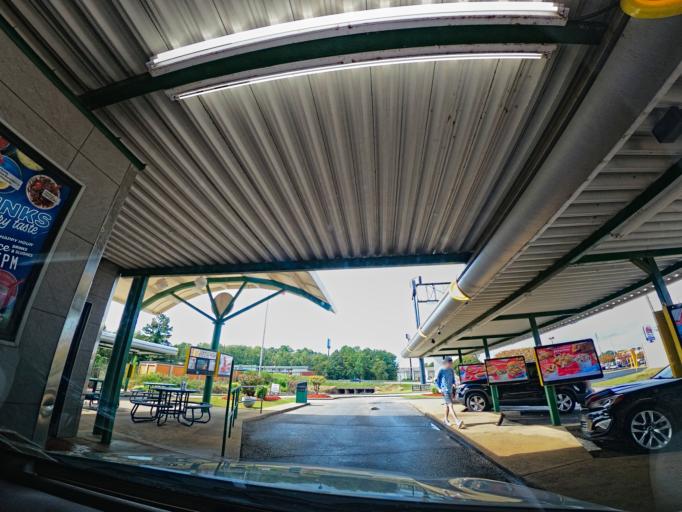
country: US
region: Alabama
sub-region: Tuscaloosa County
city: Tuscaloosa
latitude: 33.1668
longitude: -87.5242
